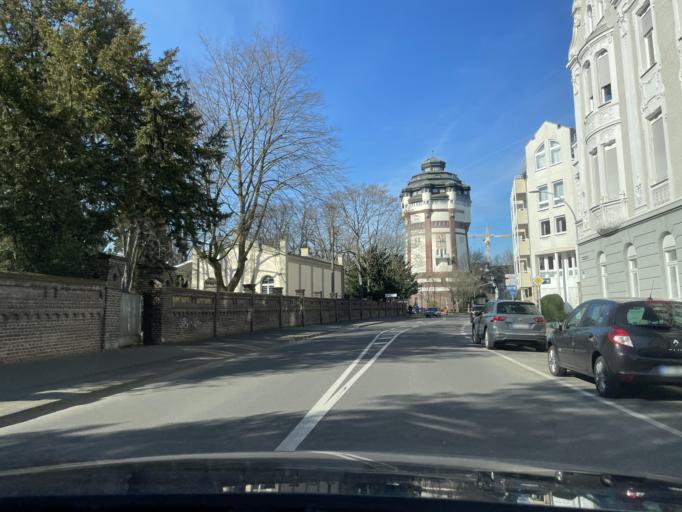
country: DE
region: North Rhine-Westphalia
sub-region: Regierungsbezirk Dusseldorf
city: Monchengladbach
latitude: 51.1998
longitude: 6.4277
